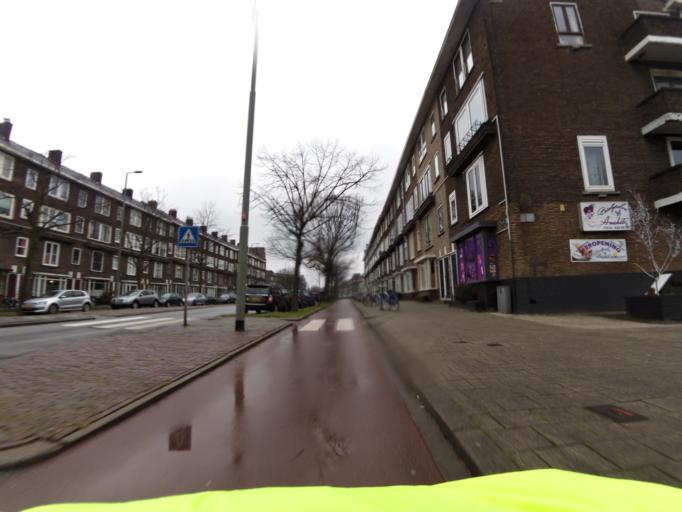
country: NL
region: South Holland
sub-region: Gemeente Schiedam
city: Schiedam
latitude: 51.9114
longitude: 4.3861
